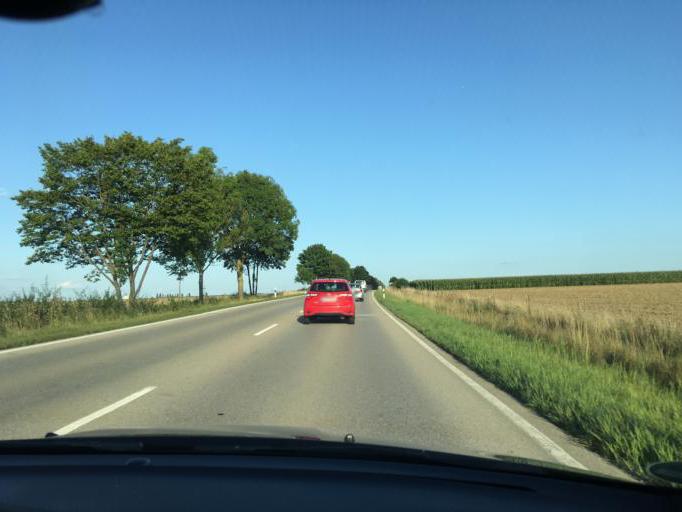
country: DE
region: Bavaria
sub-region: Upper Bavaria
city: Stammham
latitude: 48.2868
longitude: 11.8748
